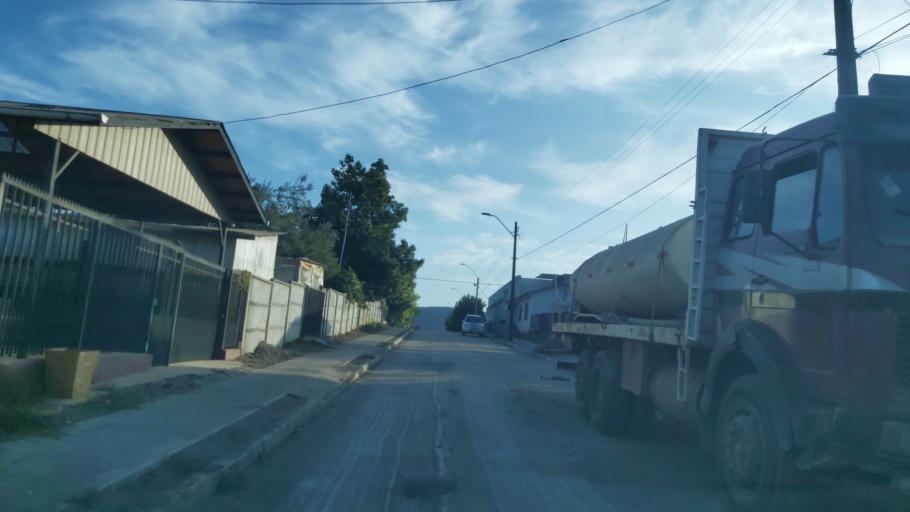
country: CL
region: Biobio
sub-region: Provincia de Biobio
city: La Laja
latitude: -37.1612
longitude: -72.9073
